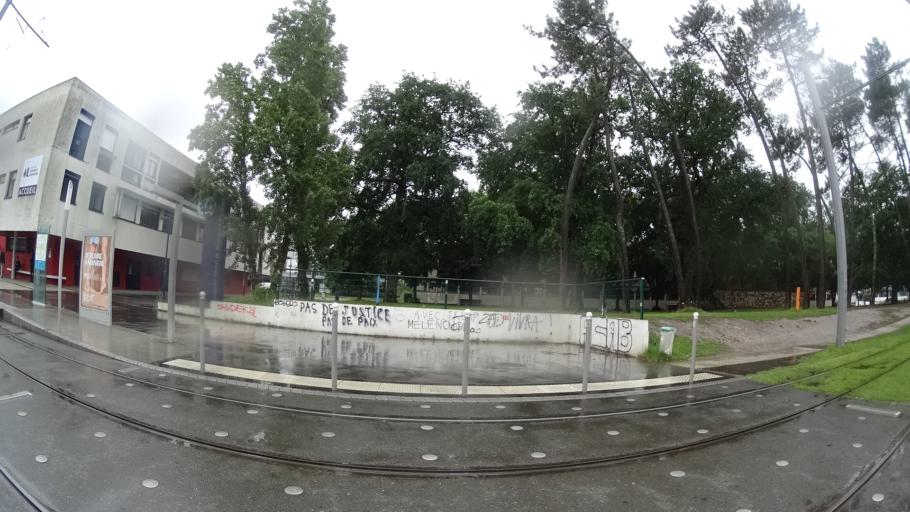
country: FR
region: Aquitaine
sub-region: Departement de la Gironde
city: Talence
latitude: 44.7967
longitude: -0.6179
